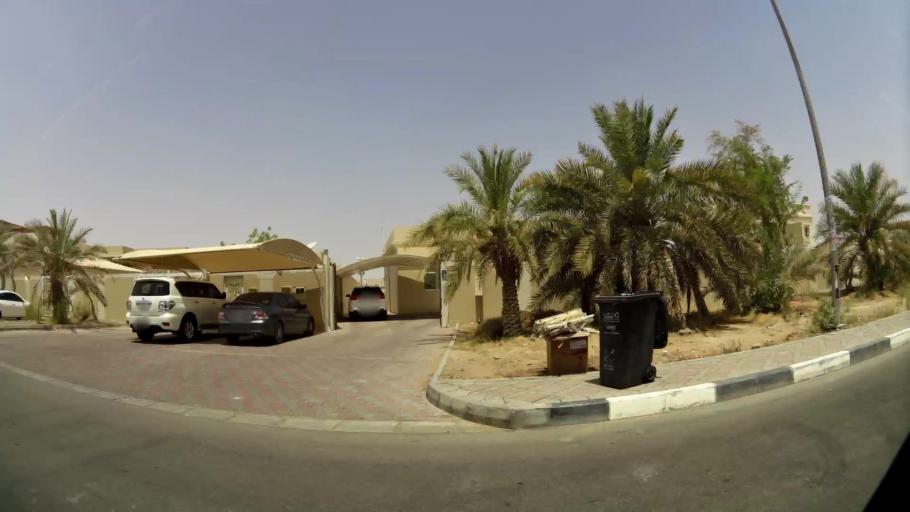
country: AE
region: Abu Dhabi
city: Al Ain
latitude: 24.1948
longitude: 55.7371
